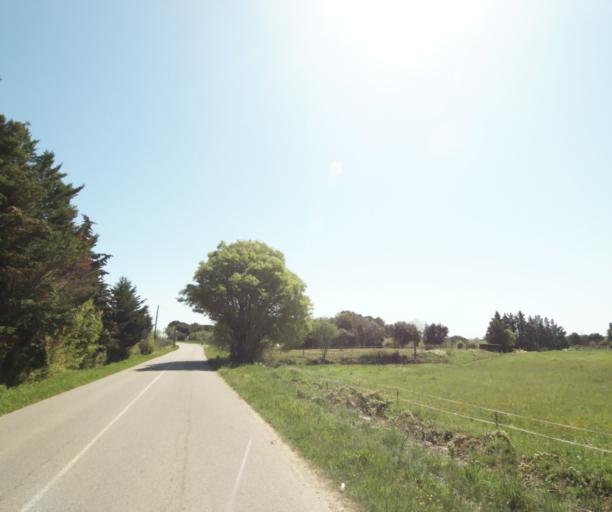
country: FR
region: Languedoc-Roussillon
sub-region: Departement de l'Herault
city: Baillargues
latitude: 43.6658
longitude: 3.9983
